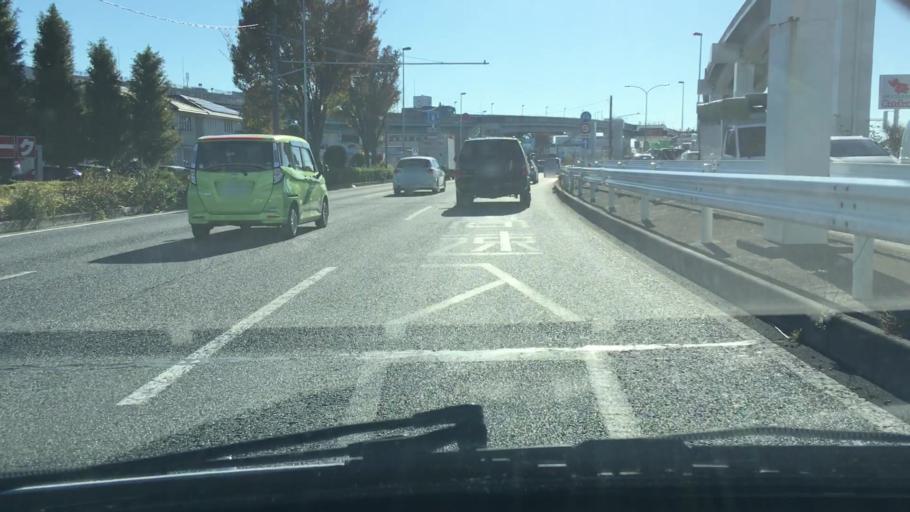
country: JP
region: Saitama
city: Yono
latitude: 35.8913
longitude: 139.6119
